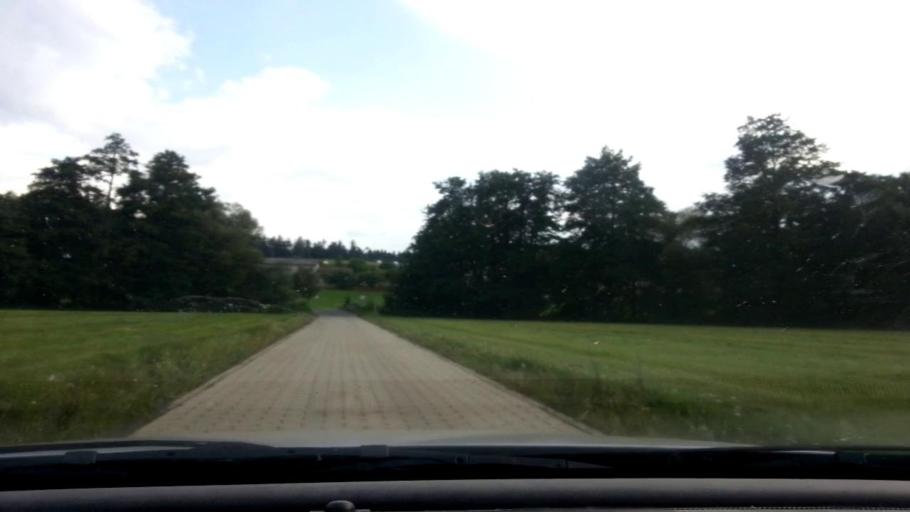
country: DE
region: Bavaria
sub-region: Upper Palatinate
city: Krummennaab
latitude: 49.8335
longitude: 12.0759
